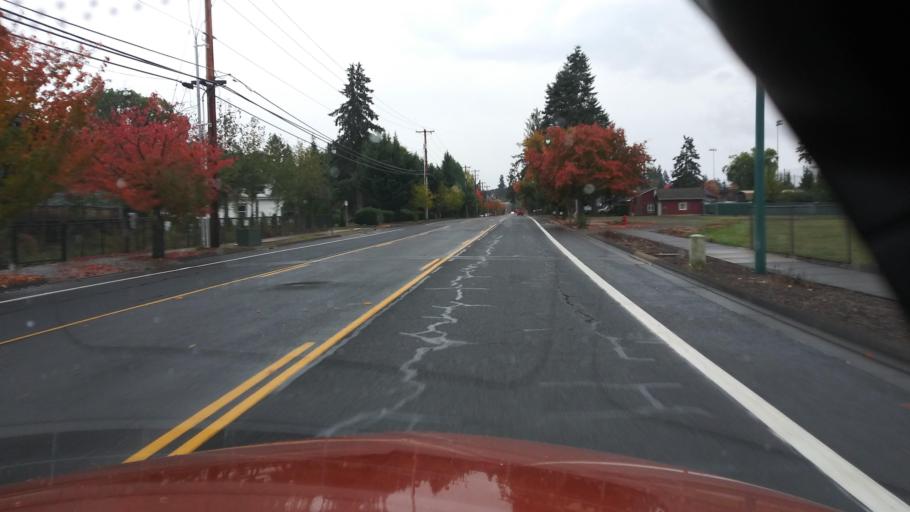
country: US
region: Oregon
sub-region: Washington County
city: Forest Grove
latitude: 45.5294
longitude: -123.1075
